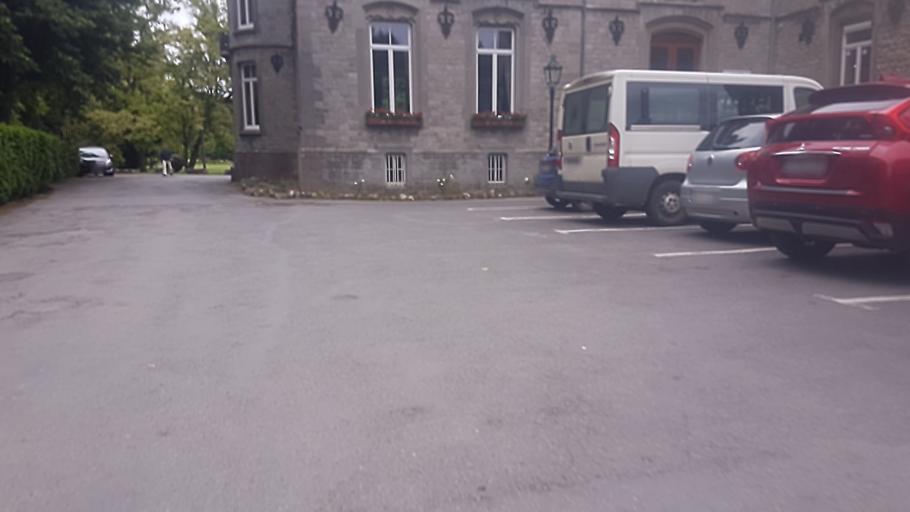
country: BE
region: Wallonia
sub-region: Province de Namur
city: Couvin
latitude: 50.0752
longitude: 4.5499
